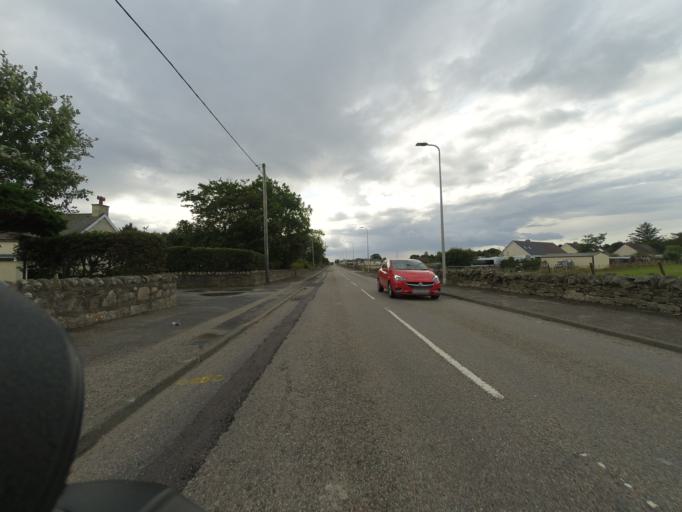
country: GB
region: Scotland
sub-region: Highland
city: Brora
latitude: 58.0202
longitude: -3.8560
